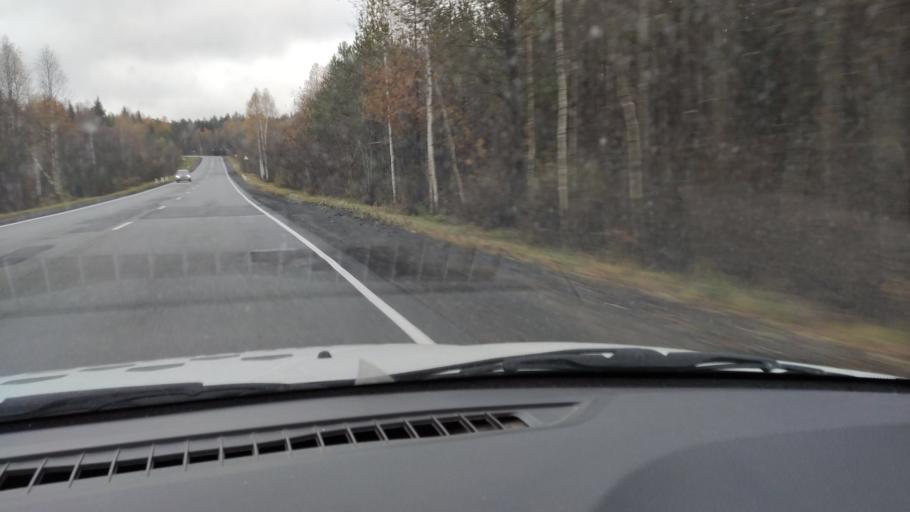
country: RU
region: Kirov
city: Dubrovka
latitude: 58.9074
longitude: 51.2538
